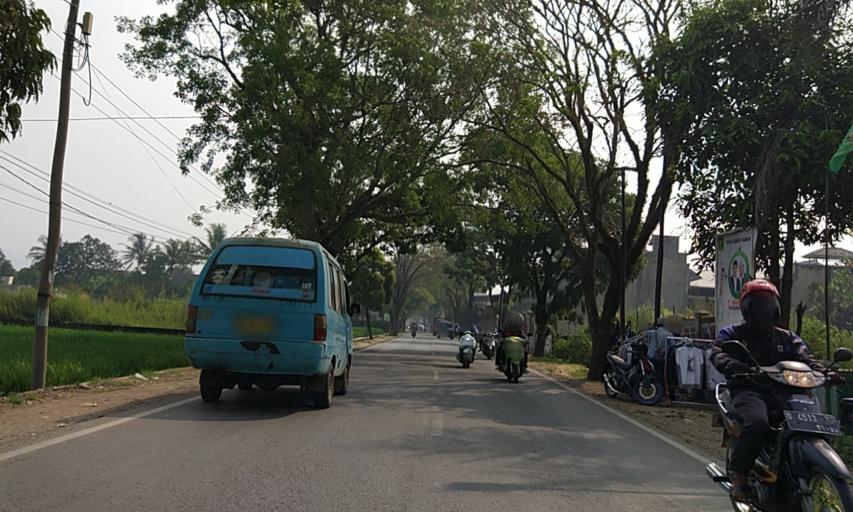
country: ID
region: West Java
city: Banjaran
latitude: -7.0443
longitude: 107.5677
